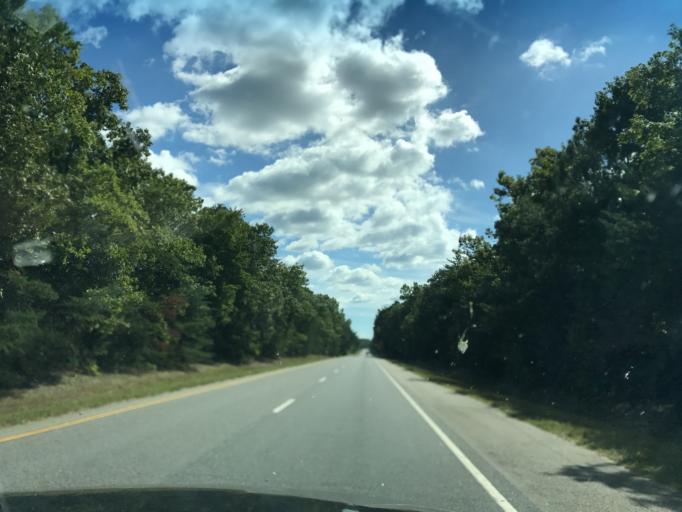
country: US
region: Virginia
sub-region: King and Queen County
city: King and Queen Court House
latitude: 37.7386
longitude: -76.7214
